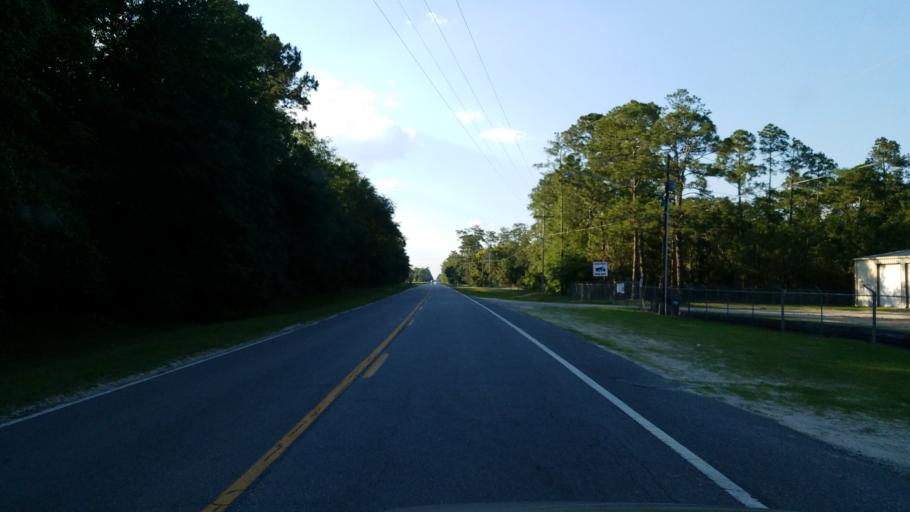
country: US
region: Georgia
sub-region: Lanier County
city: Lakeland
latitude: 31.0528
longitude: -83.0694
